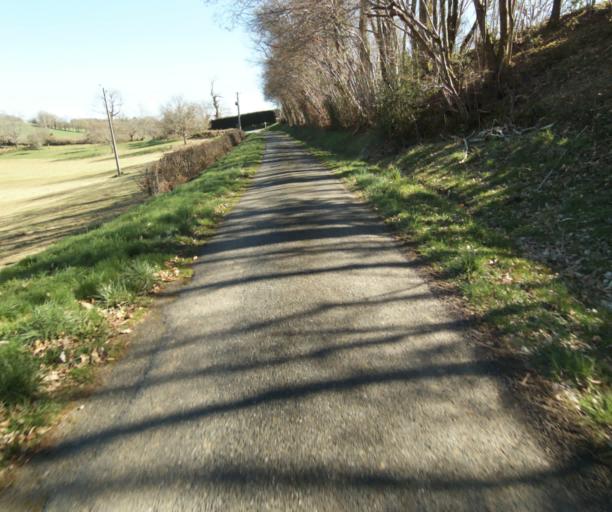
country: FR
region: Limousin
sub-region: Departement de la Correze
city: Chamboulive
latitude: 45.4207
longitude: 1.6649
